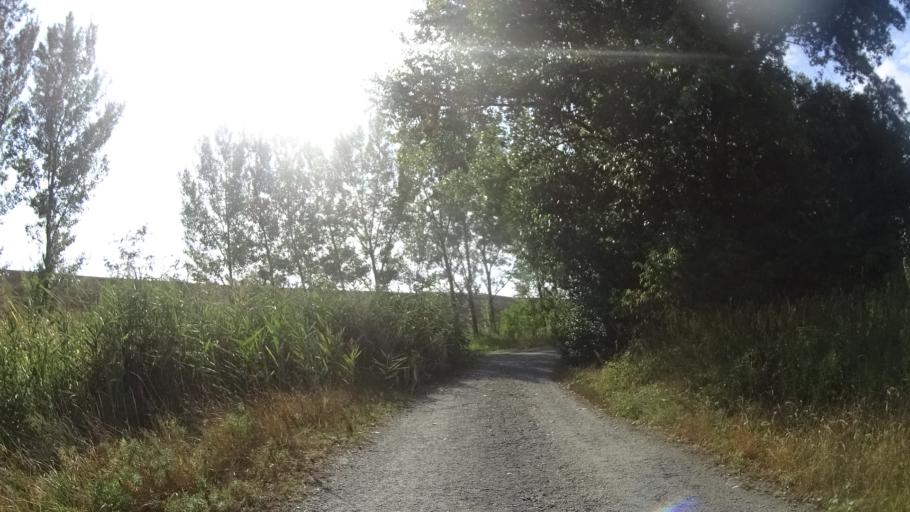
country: HU
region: Gyor-Moson-Sopron
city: Asvanyraro
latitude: 47.9280
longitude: 17.4766
